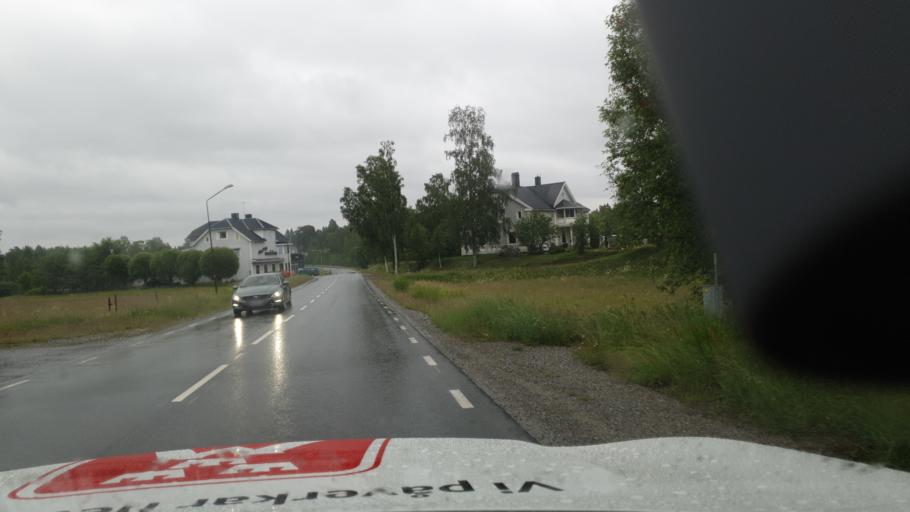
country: SE
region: Vaesterbotten
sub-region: Nordmalings Kommun
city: Nordmaling
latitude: 63.5498
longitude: 19.3898
